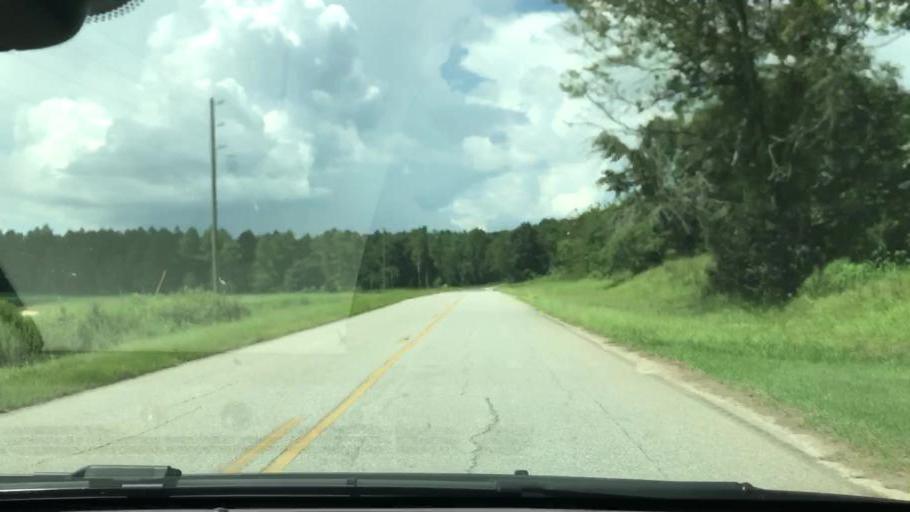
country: US
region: Georgia
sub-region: Seminole County
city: Donalsonville
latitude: 30.9899
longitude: -84.9789
